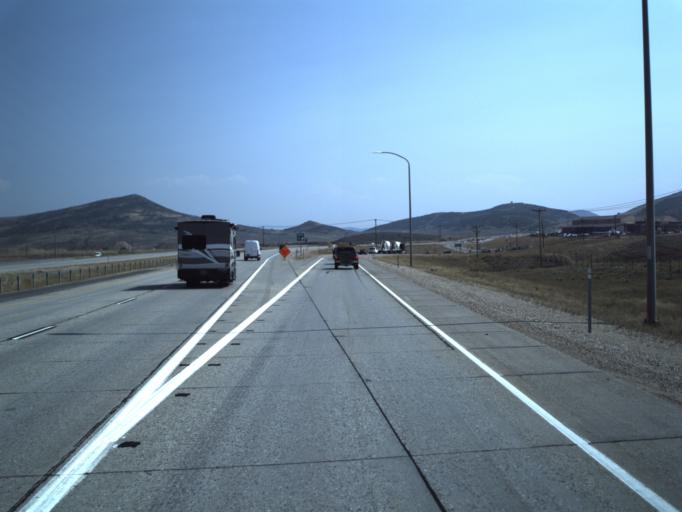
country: US
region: Utah
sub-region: Summit County
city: Park City
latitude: 40.6877
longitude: -111.4653
